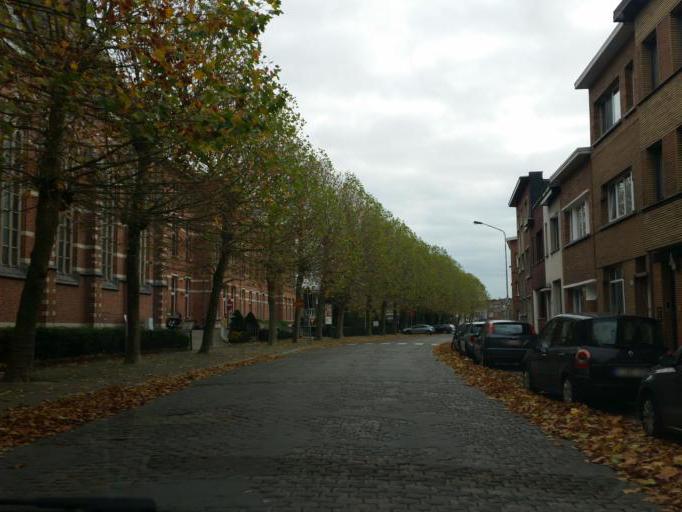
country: BE
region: Flanders
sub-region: Provincie Antwerpen
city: Mortsel
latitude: 51.1797
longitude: 4.4281
